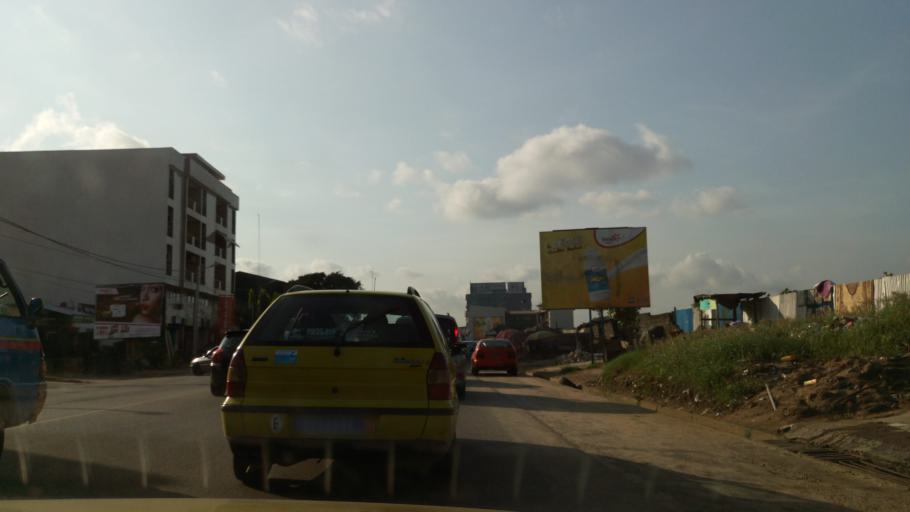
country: CI
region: Lagunes
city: Abobo
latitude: 5.3892
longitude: -3.9751
